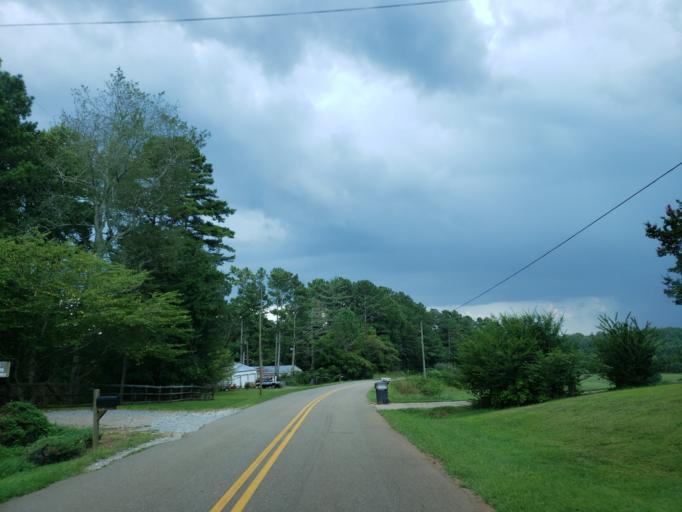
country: US
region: Georgia
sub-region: Pickens County
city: Jasper
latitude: 34.3876
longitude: -84.4657
